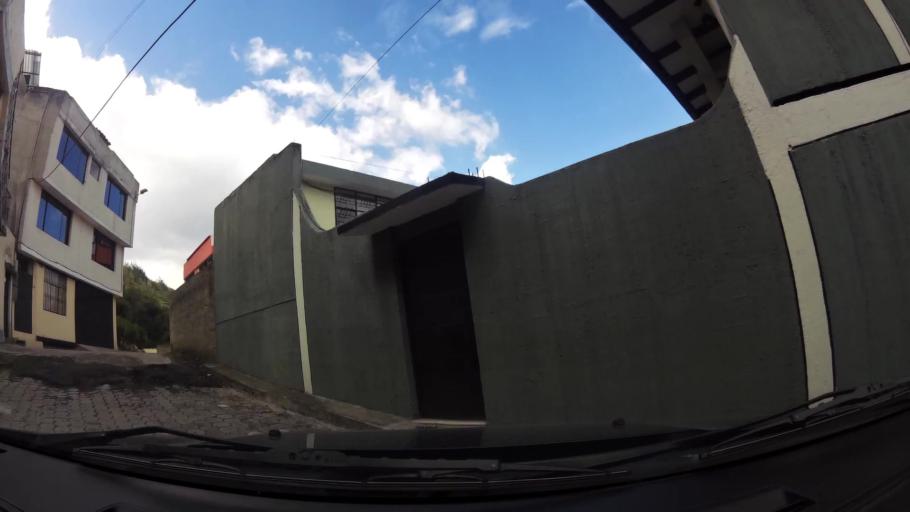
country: EC
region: Pichincha
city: Quito
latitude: -0.2278
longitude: -78.5017
